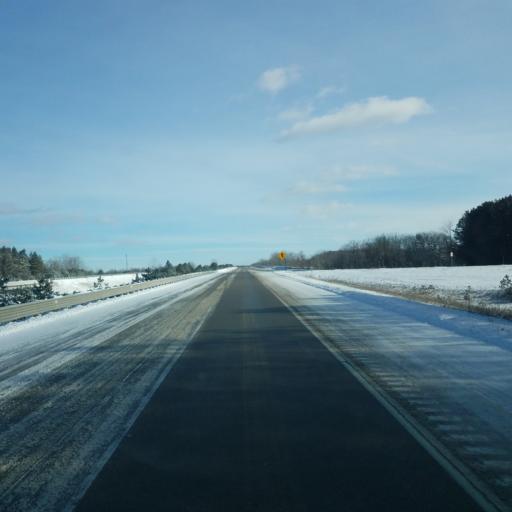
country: US
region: Michigan
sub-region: Clare County
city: Clare
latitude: 43.8620
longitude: -84.9159
